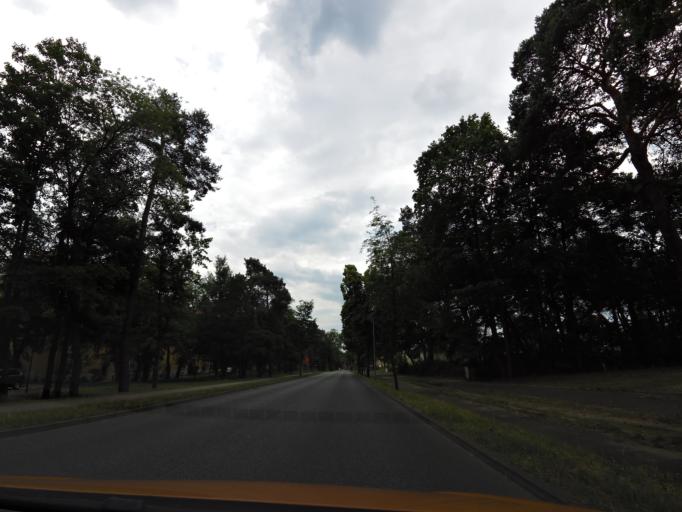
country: DE
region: Brandenburg
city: Zossen
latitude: 52.1662
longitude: 13.4728
